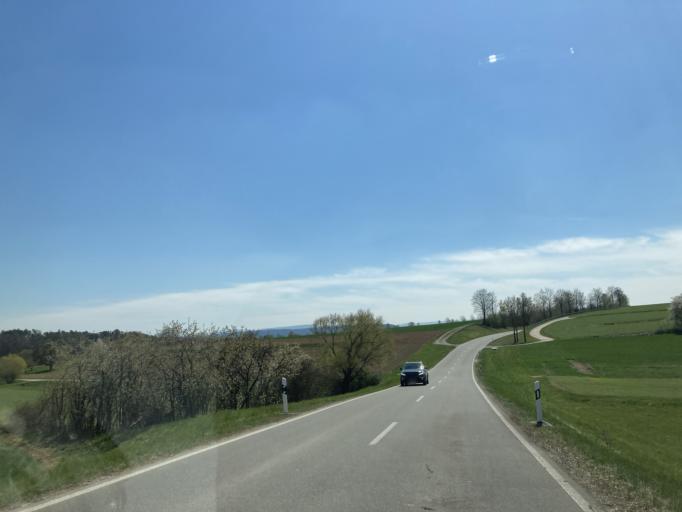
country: DE
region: Baden-Wuerttemberg
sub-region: Regierungsbezirk Stuttgart
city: Bondorf
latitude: 48.5031
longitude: 8.8738
